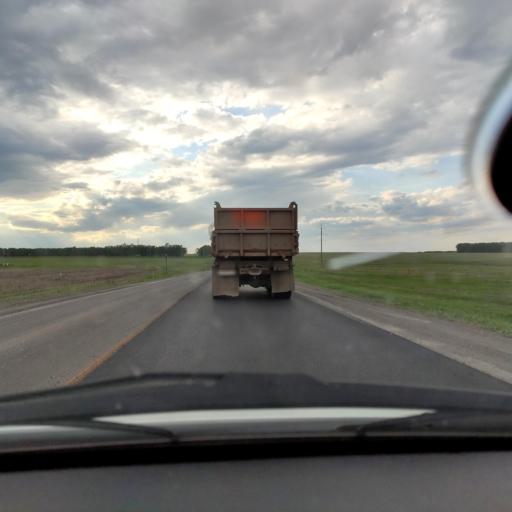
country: RU
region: Bashkortostan
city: Dyurtyuli
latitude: 55.3239
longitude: 54.9726
